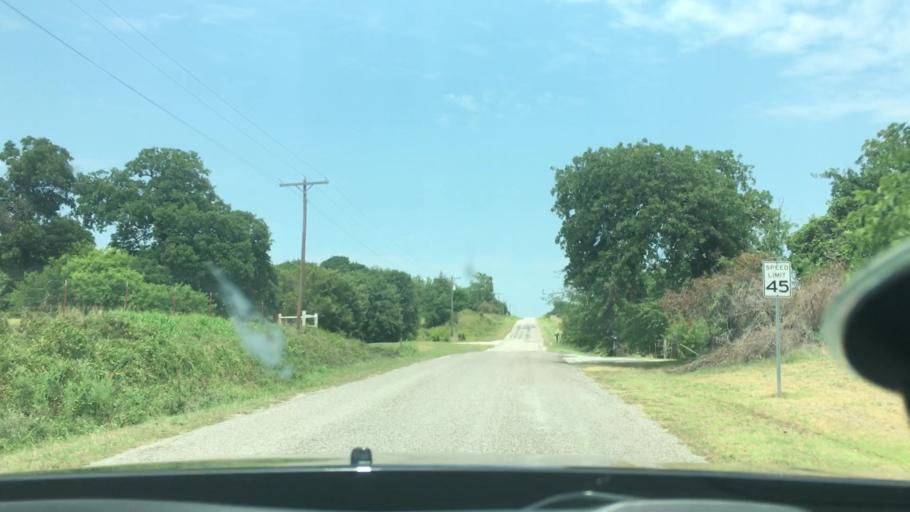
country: US
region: Oklahoma
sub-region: Love County
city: Marietta
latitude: 33.8926
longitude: -97.3522
